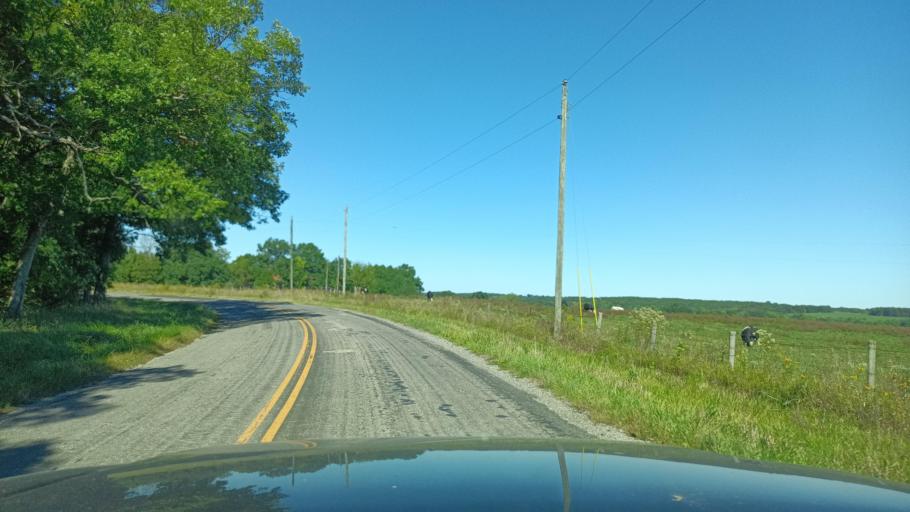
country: US
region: Missouri
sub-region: Scotland County
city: Memphis
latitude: 40.3556
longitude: -92.2577
